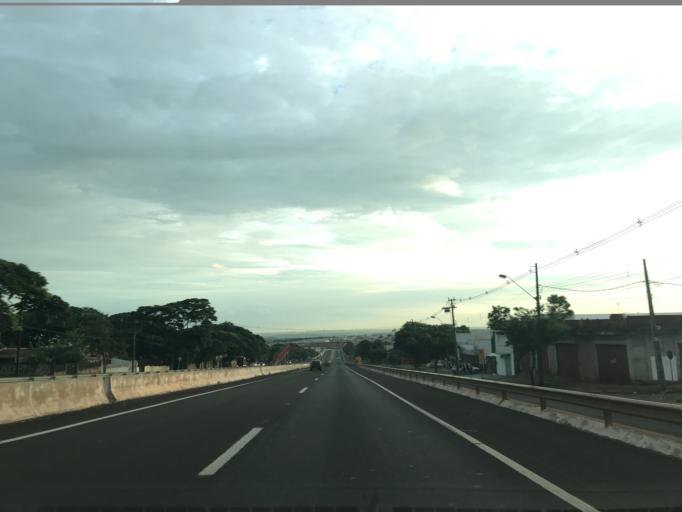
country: BR
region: Parana
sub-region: Maringa
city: Maringa
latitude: -23.4016
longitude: -51.9797
